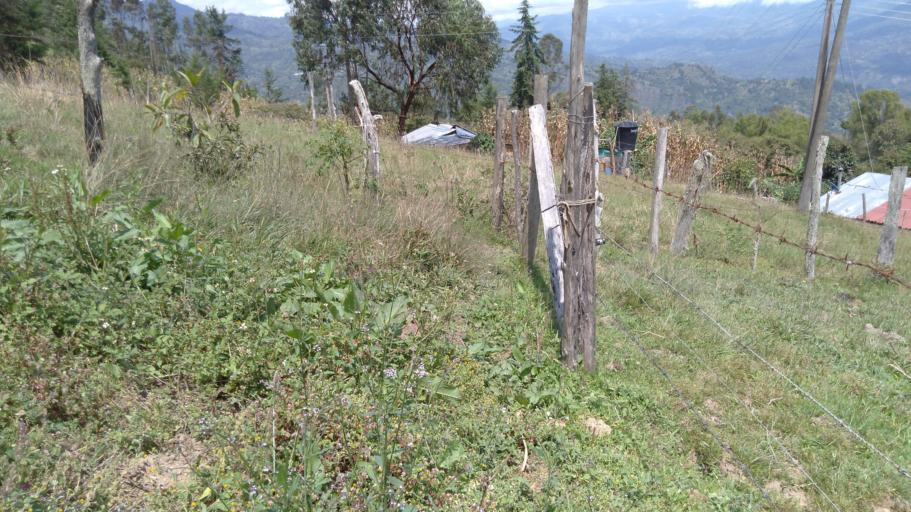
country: CO
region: Cundinamarca
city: Tenza
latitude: 5.0609
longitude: -73.4340
